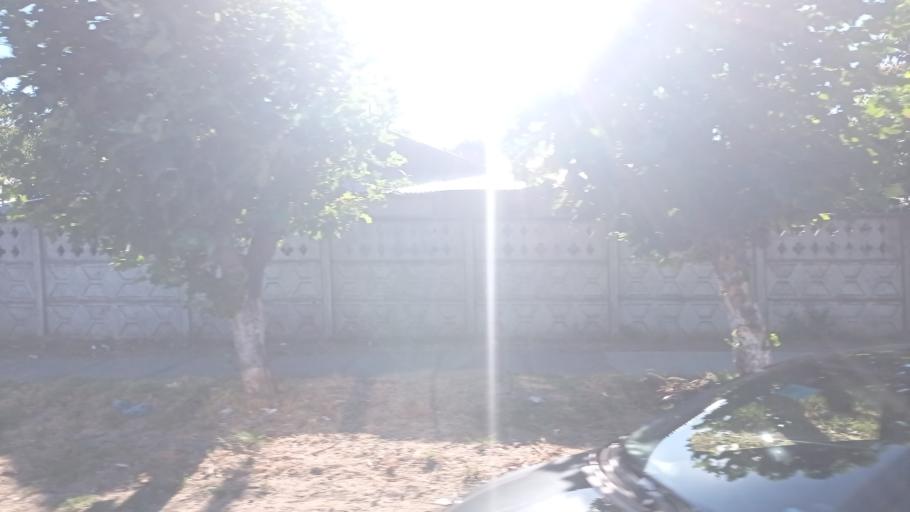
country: CL
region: Biobio
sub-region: Provincia de Biobio
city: Nacimiento
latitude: -37.5581
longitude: -72.5950
